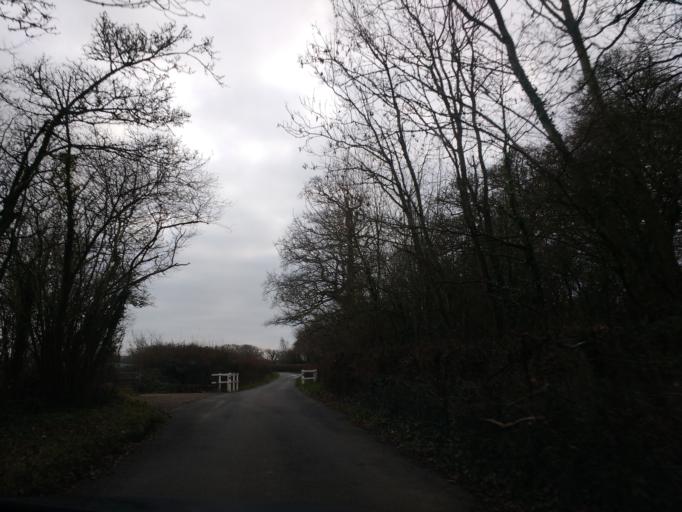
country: GB
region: England
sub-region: Isle of Wight
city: Shalfleet
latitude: 50.6964
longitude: -1.3947
